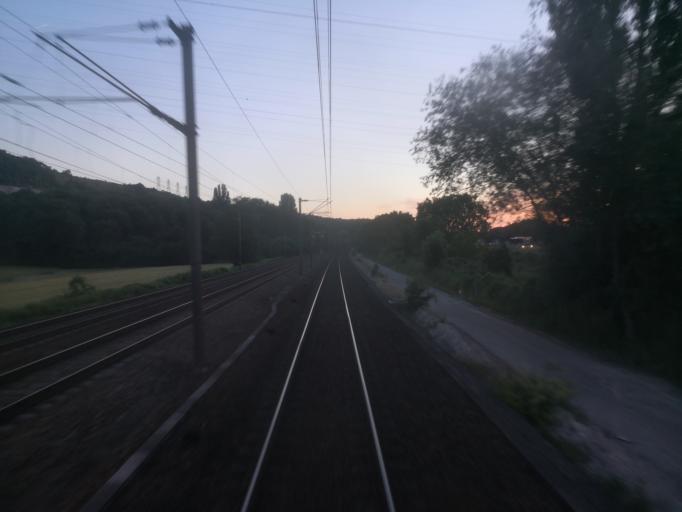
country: FR
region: Ile-de-France
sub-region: Departement des Yvelines
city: Porcheville
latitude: 48.9635
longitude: 1.7729
